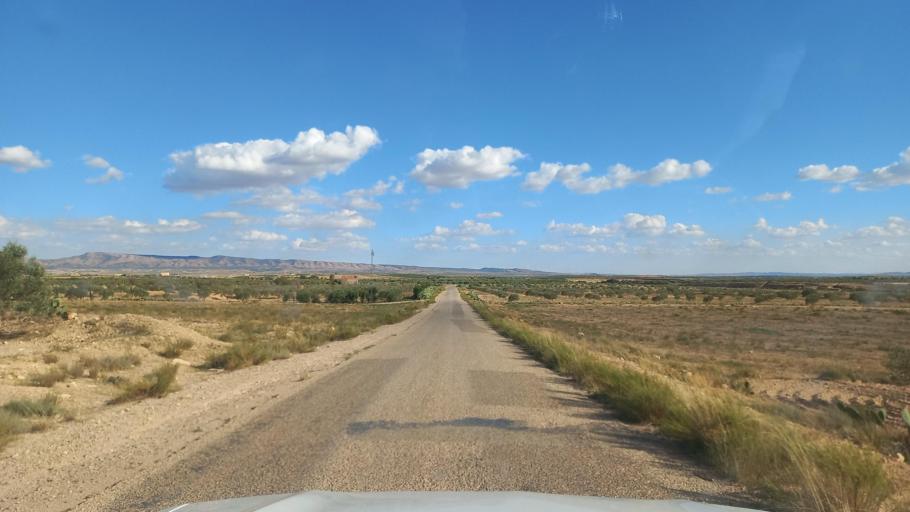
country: TN
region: Al Qasrayn
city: Sbiba
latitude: 35.3892
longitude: 9.0276
